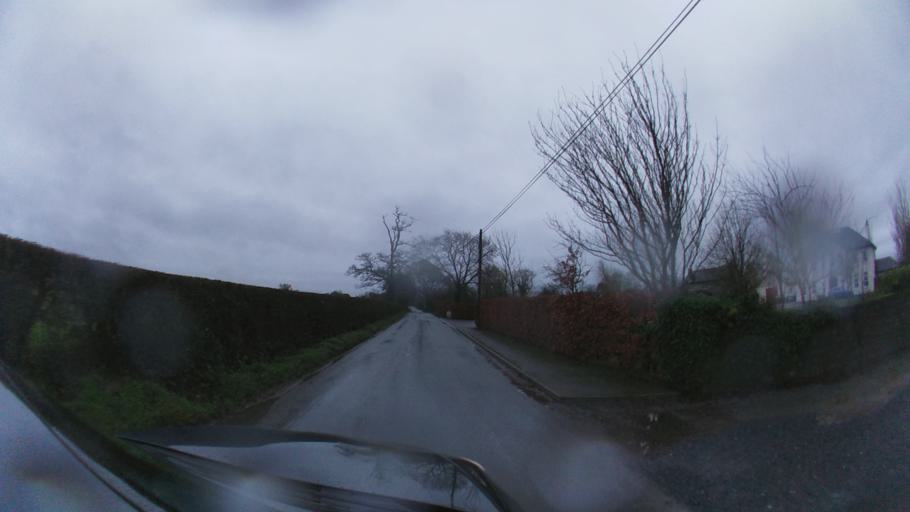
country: IE
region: Leinster
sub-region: County Carlow
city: Bagenalstown
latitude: 52.6670
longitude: -6.9995
